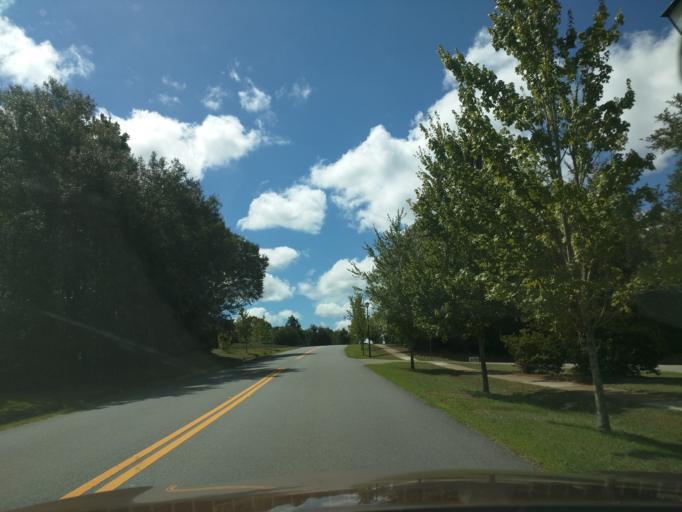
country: US
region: Florida
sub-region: Leon County
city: Tallahassee
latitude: 30.5840
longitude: -84.2548
